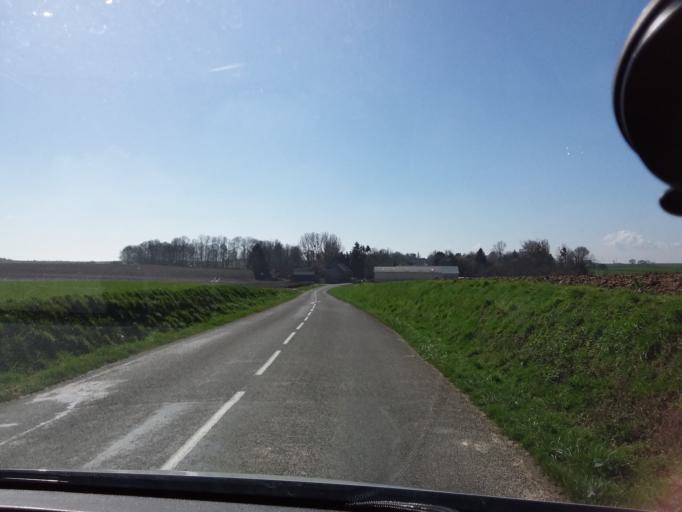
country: FR
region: Picardie
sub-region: Departement de l'Aisne
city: Montcornet
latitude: 49.7618
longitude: 4.0038
